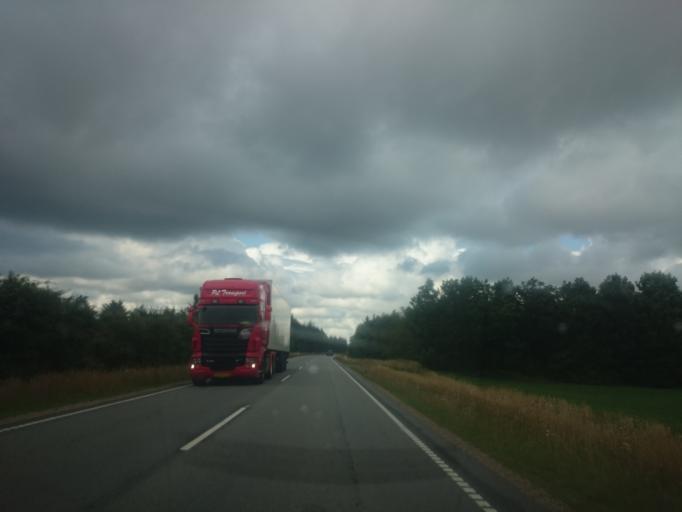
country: DK
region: South Denmark
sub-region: Billund Kommune
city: Grindsted
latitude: 55.6806
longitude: 8.9609
